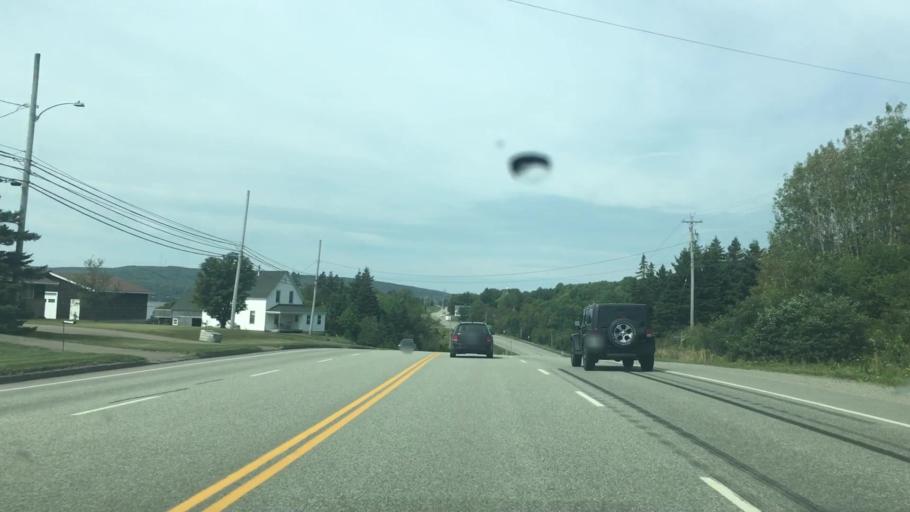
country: CA
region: Nova Scotia
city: Port Hawkesbury
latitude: 45.6427
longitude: -61.3927
